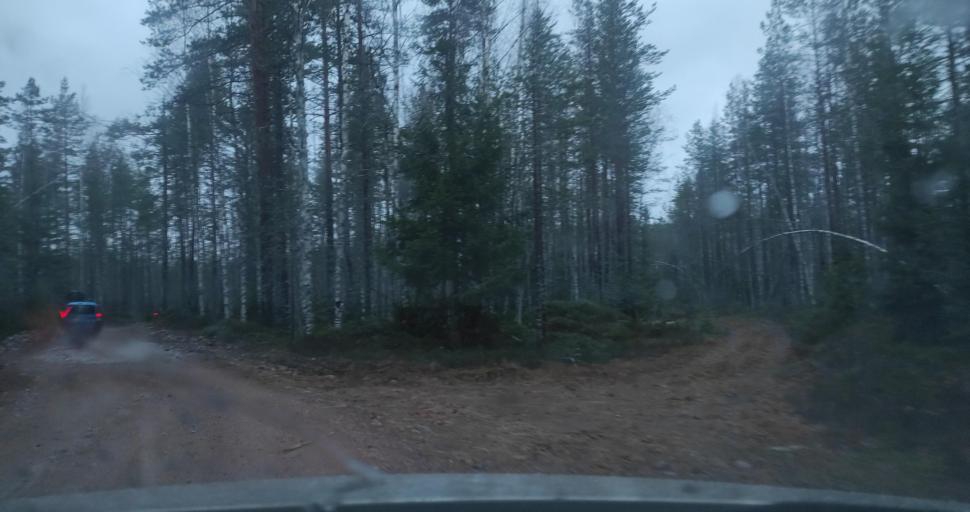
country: RU
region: Republic of Karelia
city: Salmi
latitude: 61.6279
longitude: 31.8129
